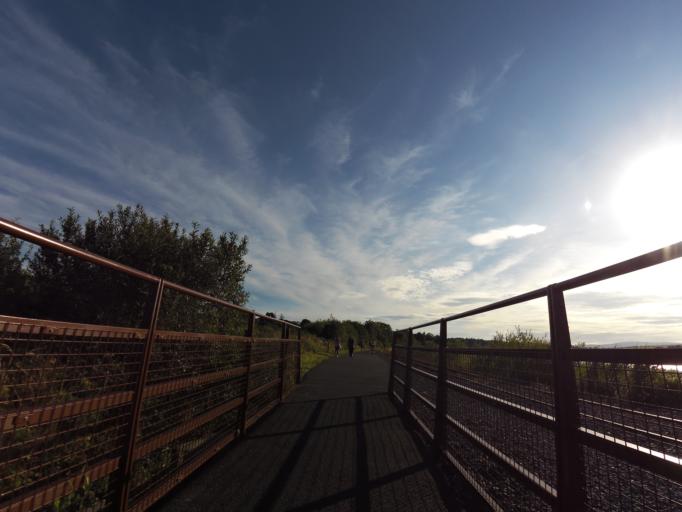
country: IE
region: Leinster
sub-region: Kilkenny
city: Mooncoin
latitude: 52.2469
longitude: -7.1995
